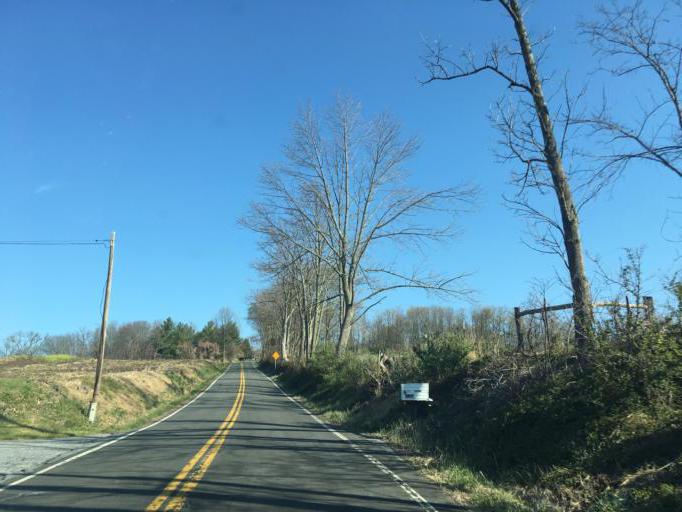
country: US
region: Maryland
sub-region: Frederick County
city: Myersville
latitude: 39.5418
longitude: -77.5458
